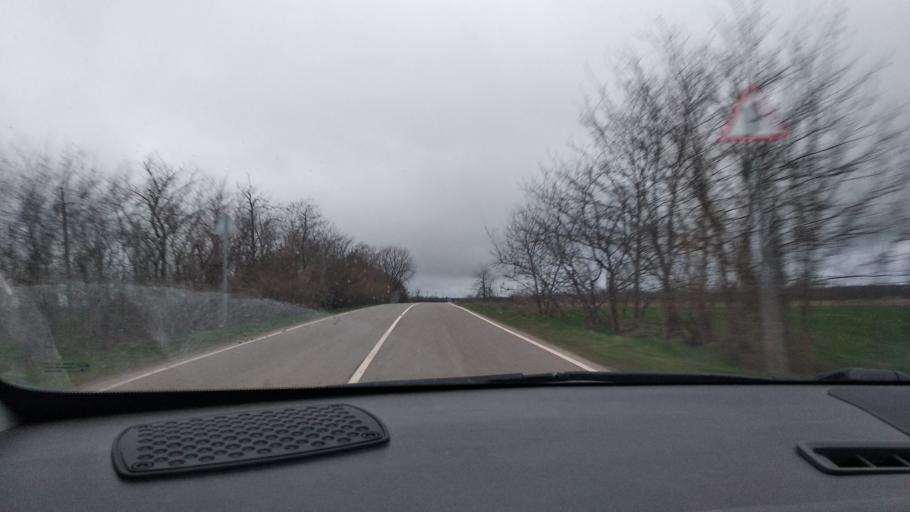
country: RU
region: Krasnodarskiy
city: Afipskiy
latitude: 44.8994
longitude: 38.7895
